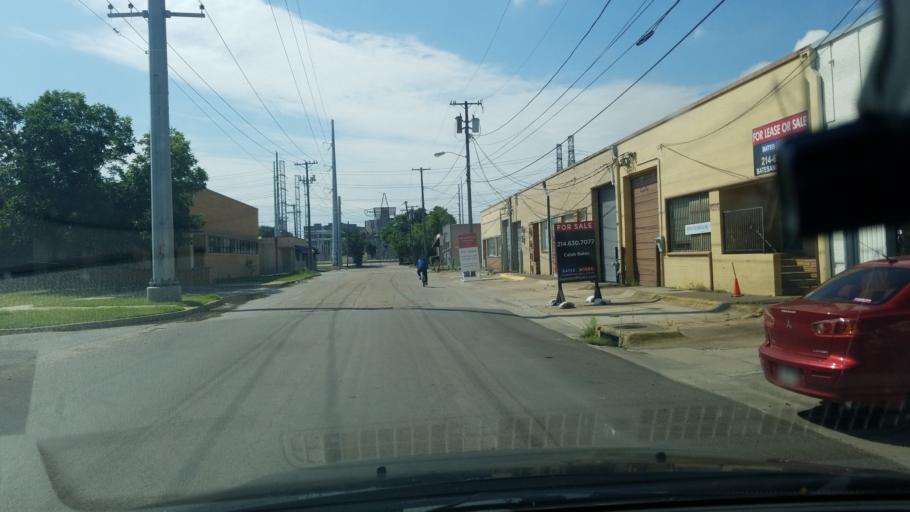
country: US
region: Texas
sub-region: Dallas County
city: Dallas
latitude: 32.7857
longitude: -96.8213
